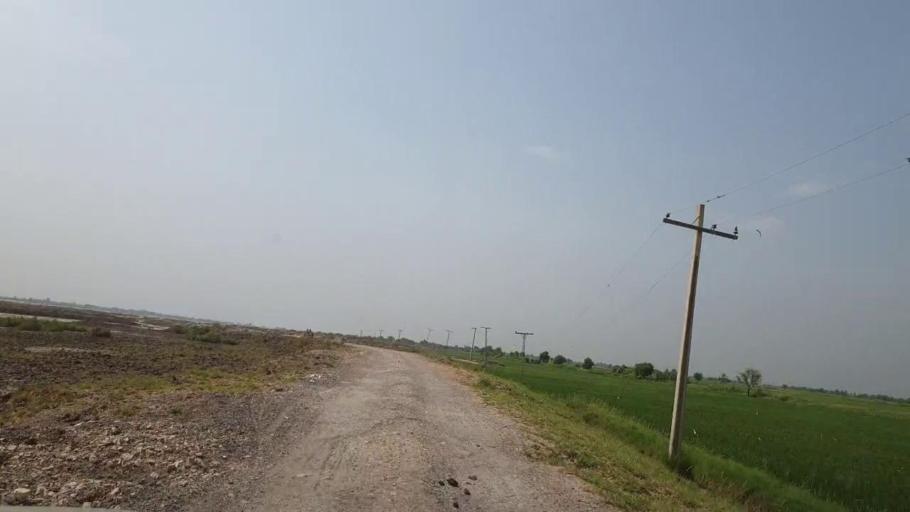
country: PK
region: Sindh
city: Dokri
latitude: 27.4255
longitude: 68.2040
